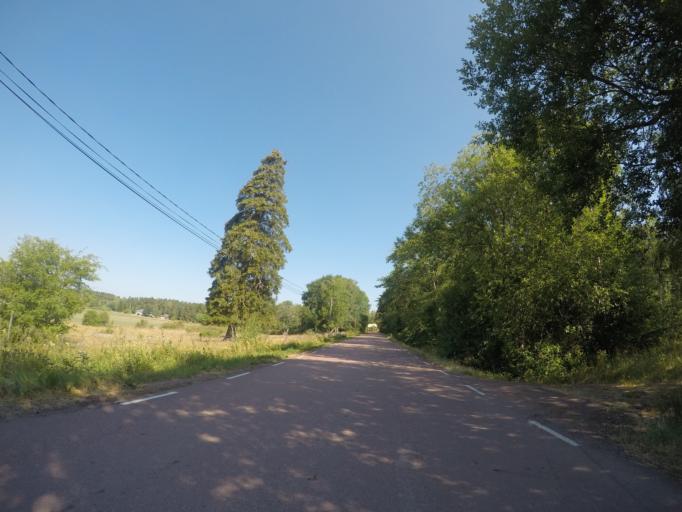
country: AX
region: Alands landsbygd
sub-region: Jomala
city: Jomala
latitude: 60.2094
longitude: 19.9738
